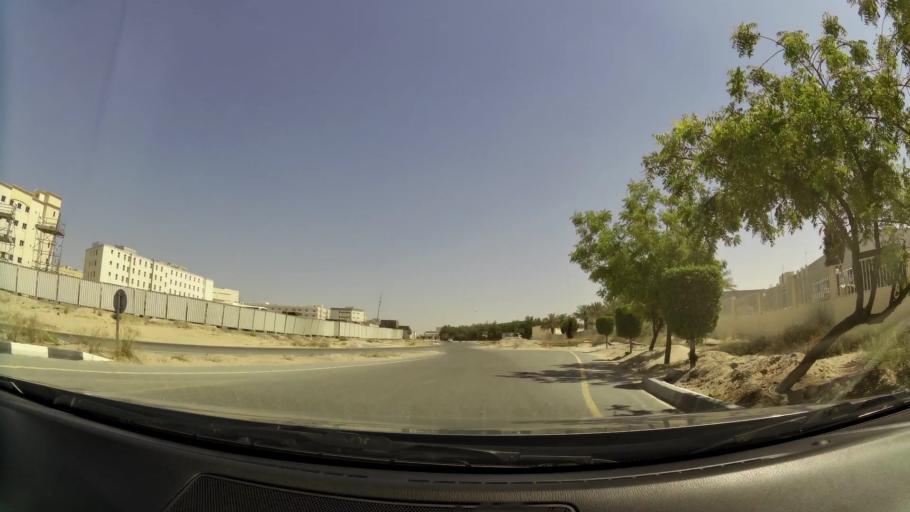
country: AE
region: Dubai
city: Dubai
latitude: 24.9719
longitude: 55.2076
